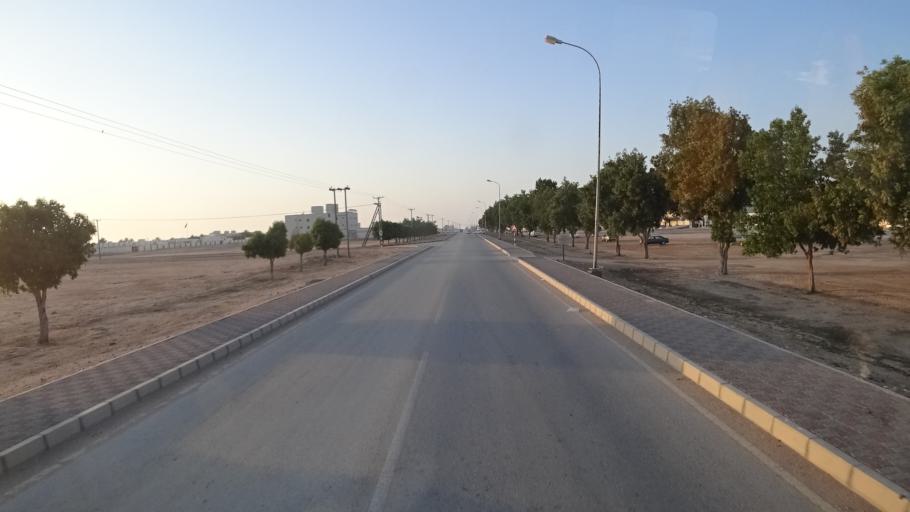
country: OM
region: Ash Sharqiyah
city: Sur
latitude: 22.5184
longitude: 59.7929
